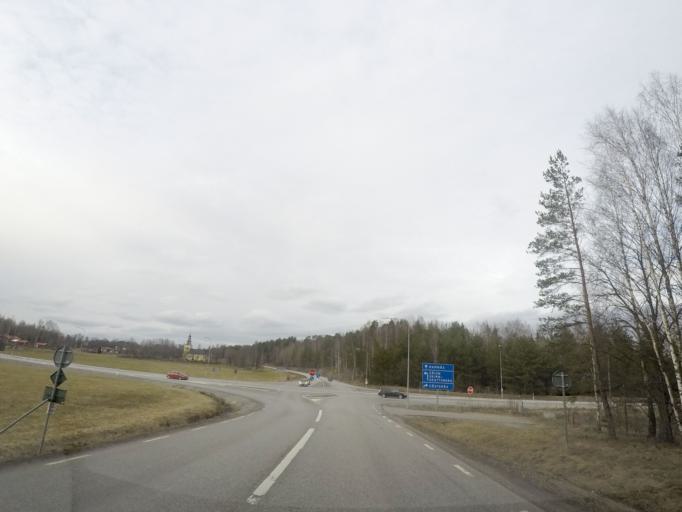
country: SE
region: Vaestmanland
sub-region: Surahammars Kommun
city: Ramnas
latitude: 59.7579
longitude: 16.2108
